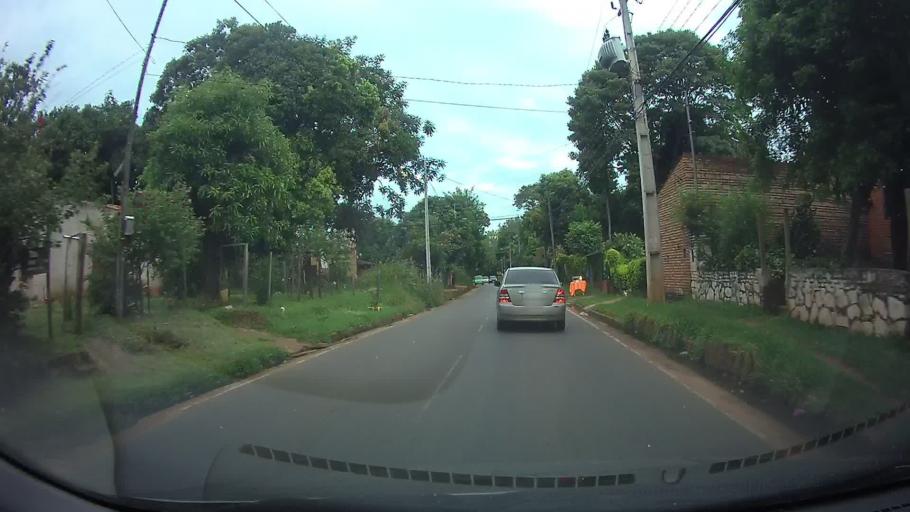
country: PY
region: Central
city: San Lorenzo
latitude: -25.3029
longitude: -57.4961
